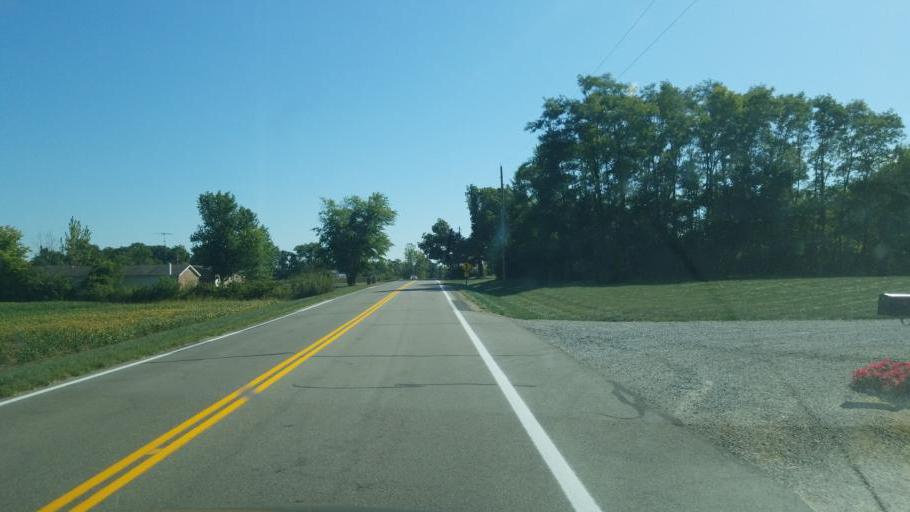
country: US
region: Ohio
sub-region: Champaign County
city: Mechanicsburg
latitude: 40.1132
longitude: -83.5833
